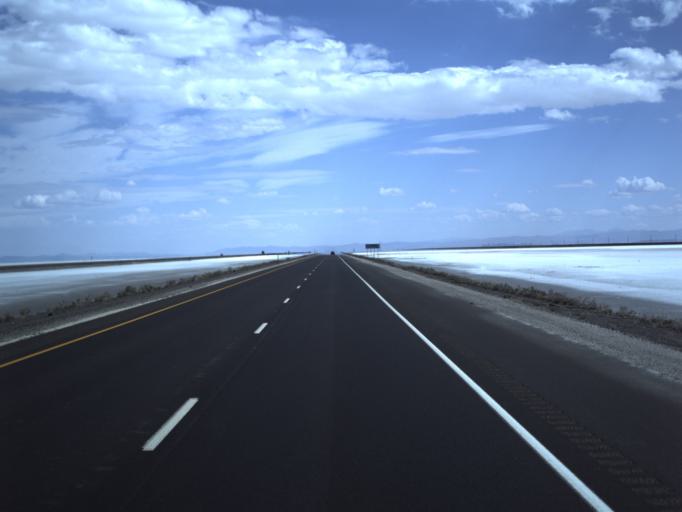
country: US
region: Utah
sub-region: Tooele County
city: Wendover
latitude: 40.7343
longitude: -113.6509
